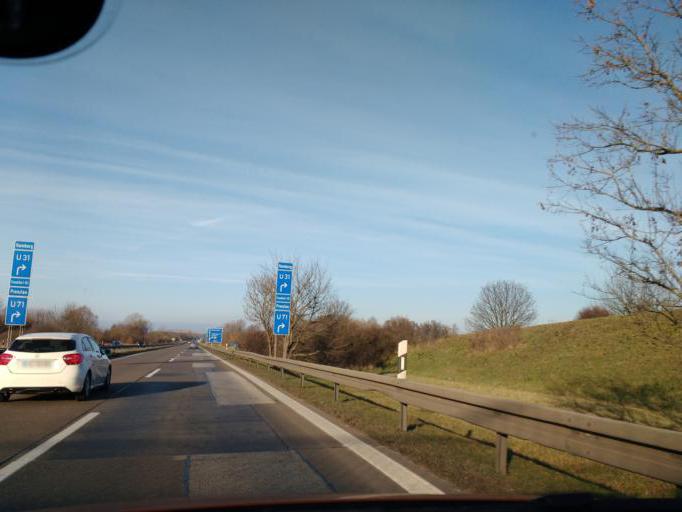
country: DE
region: Berlin
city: Buchholz
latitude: 52.6152
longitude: 13.4441
